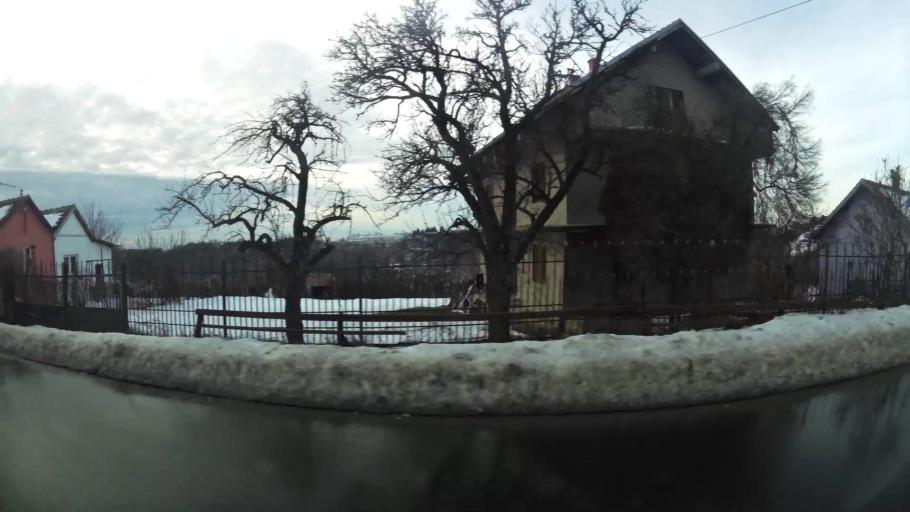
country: RS
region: Central Serbia
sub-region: Belgrade
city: Zvezdara
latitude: 44.7355
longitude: 20.5116
